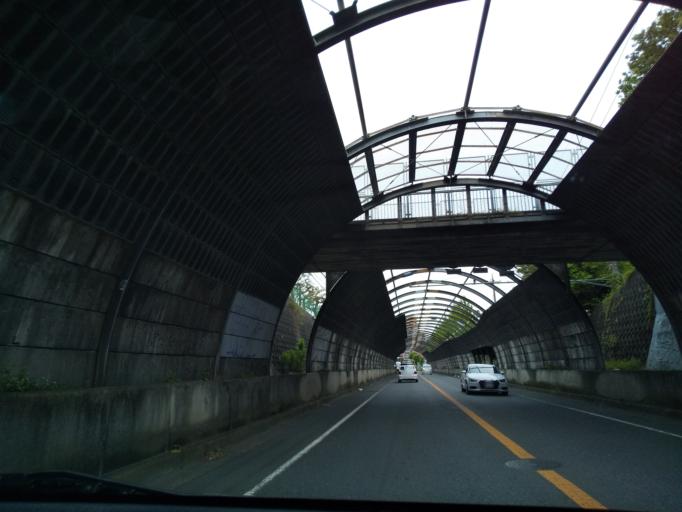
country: JP
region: Kanagawa
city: Zama
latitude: 35.5105
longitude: 139.4113
